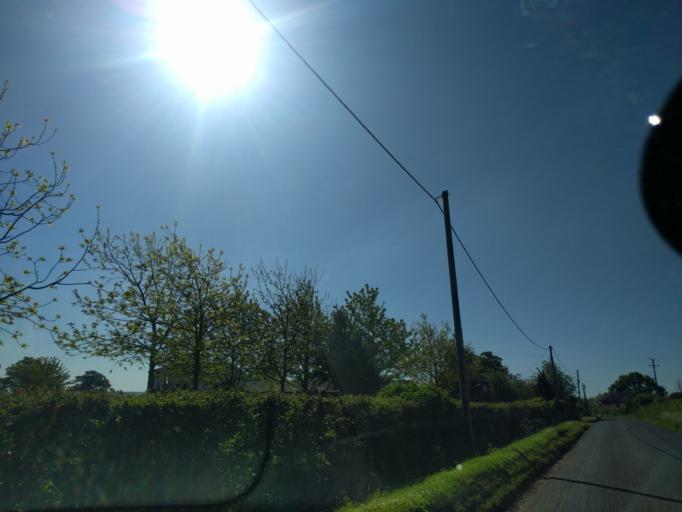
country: GB
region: England
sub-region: Wiltshire
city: Bratton
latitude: 51.2915
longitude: -2.1304
